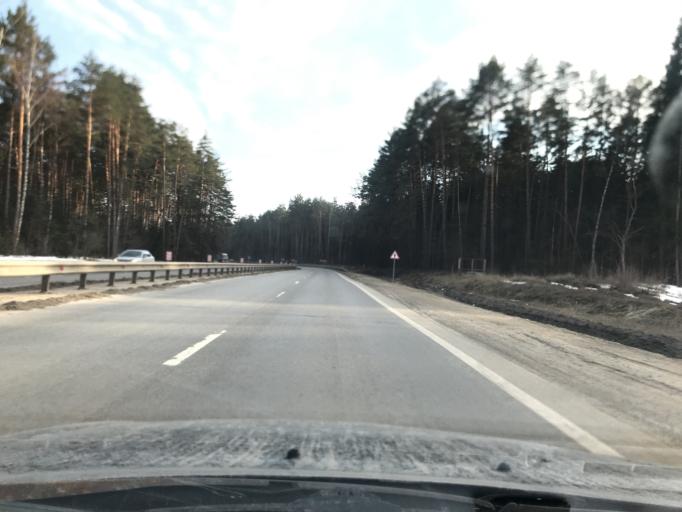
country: RU
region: Kaluga
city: Kaluga
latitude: 54.4153
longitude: 36.1998
